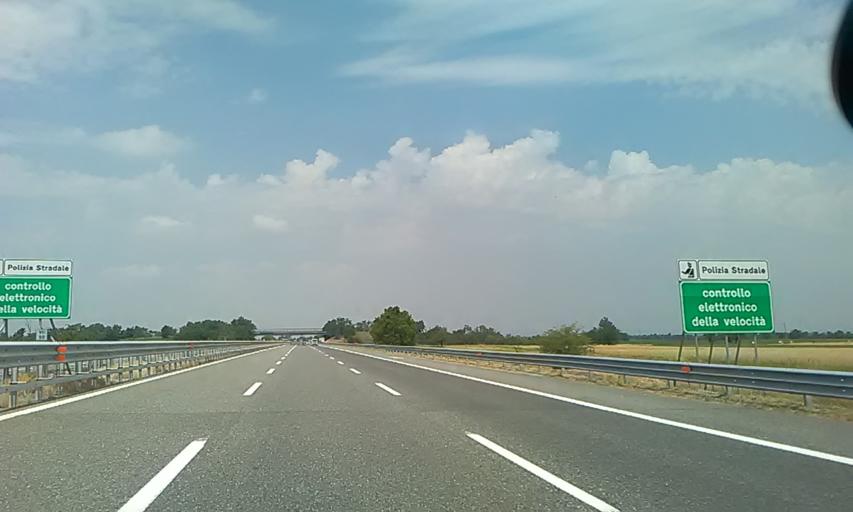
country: IT
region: Piedmont
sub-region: Provincia di Alessandria
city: Castelspina
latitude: 44.8010
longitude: 8.6059
